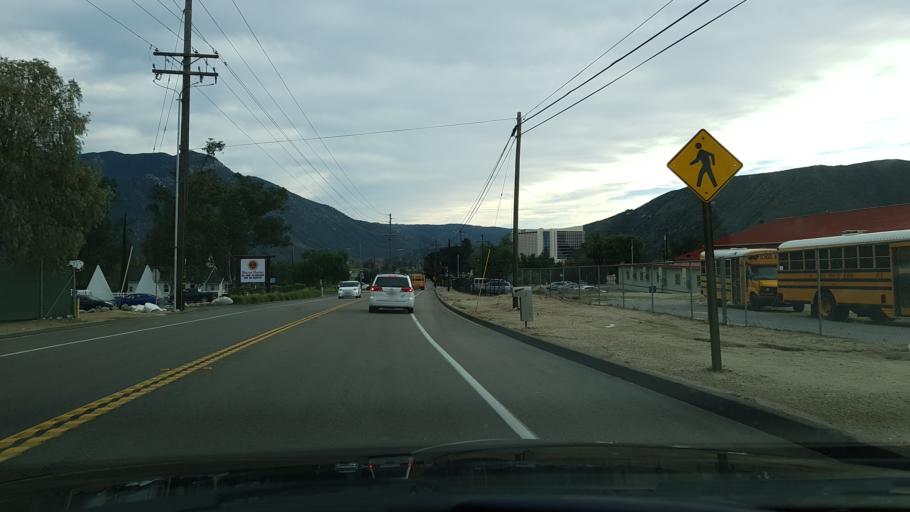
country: US
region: California
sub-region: San Diego County
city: Valley Center
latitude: 33.2788
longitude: -116.9537
